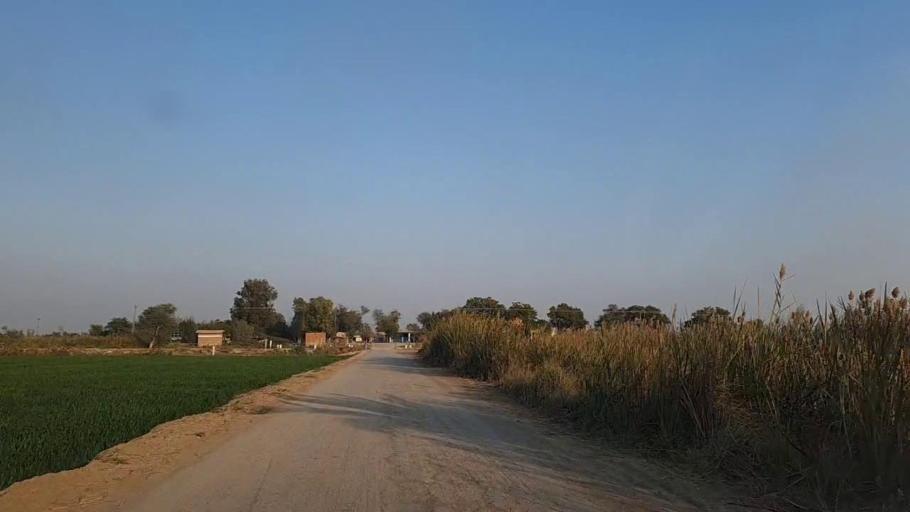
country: PK
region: Sindh
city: Daur
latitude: 26.5104
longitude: 68.3071
